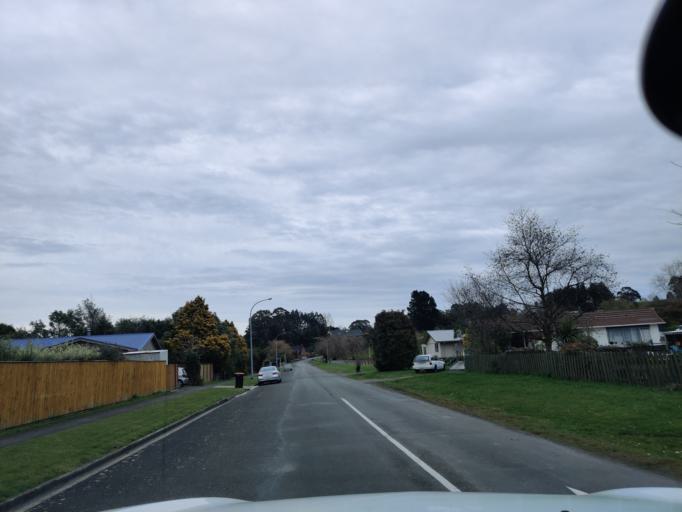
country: NZ
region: Manawatu-Wanganui
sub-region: Palmerston North City
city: Palmerston North
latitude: -40.2841
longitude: 175.7505
